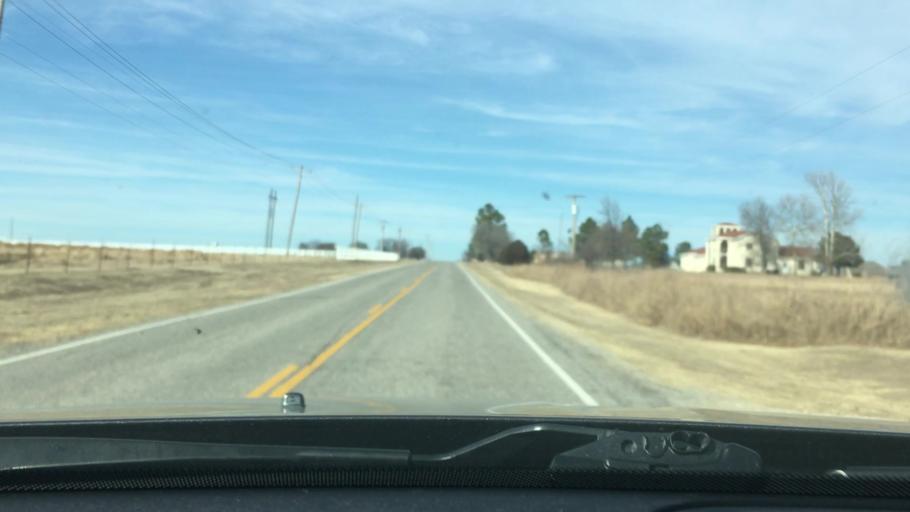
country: US
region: Oklahoma
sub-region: Murray County
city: Davis
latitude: 34.4934
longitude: -97.0905
